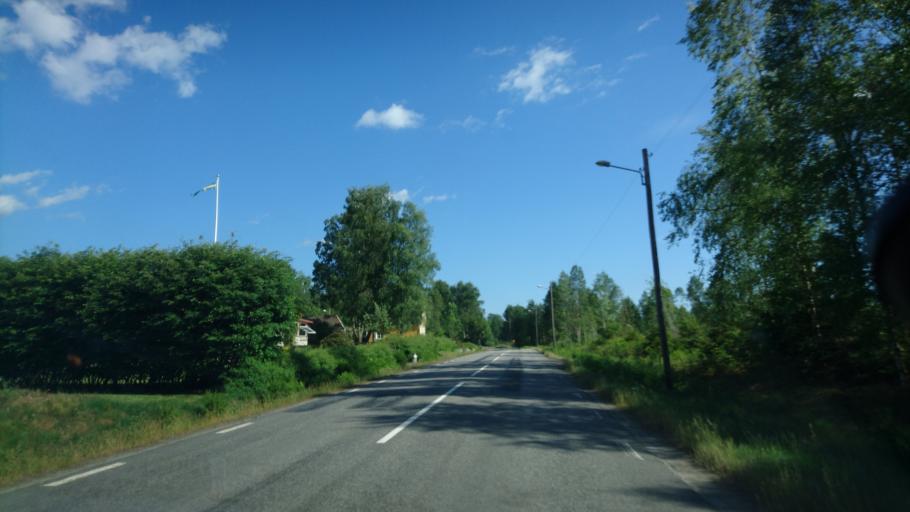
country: SE
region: Kronoberg
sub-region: Almhults Kommun
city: AElmhult
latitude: 56.4719
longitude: 14.2238
